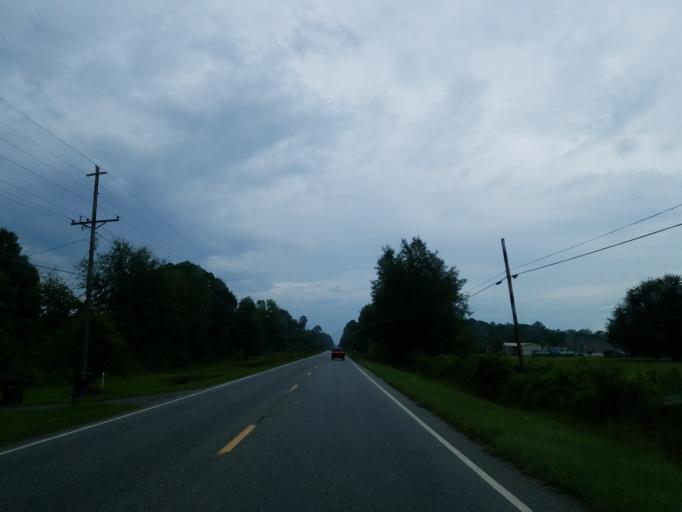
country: US
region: Georgia
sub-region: Lanier County
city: Lakeland
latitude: 31.0514
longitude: -83.1314
